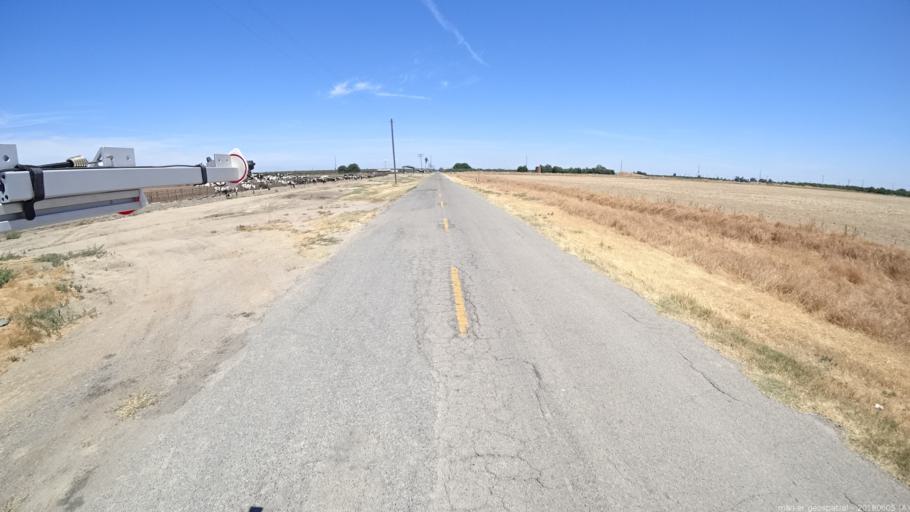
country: US
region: California
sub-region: Madera County
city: Chowchilla
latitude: 37.0907
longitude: -120.3154
